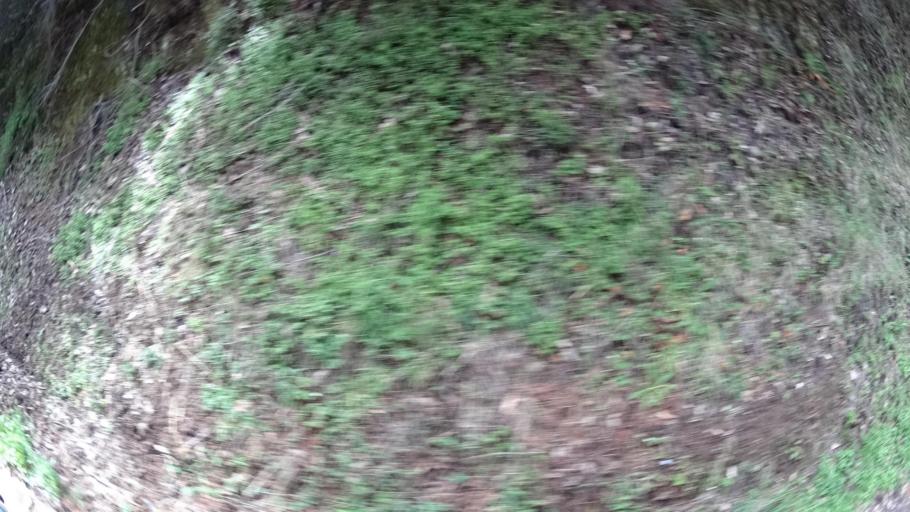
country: US
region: California
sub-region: Humboldt County
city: Blue Lake
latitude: 40.7661
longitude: -123.9347
